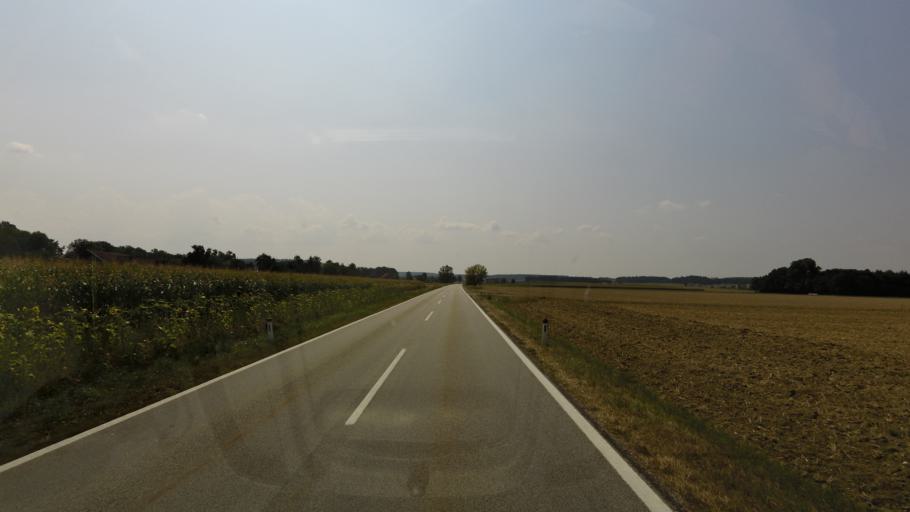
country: DE
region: Bavaria
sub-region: Lower Bavaria
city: Bad Fussing
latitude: 48.2801
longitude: 13.3289
